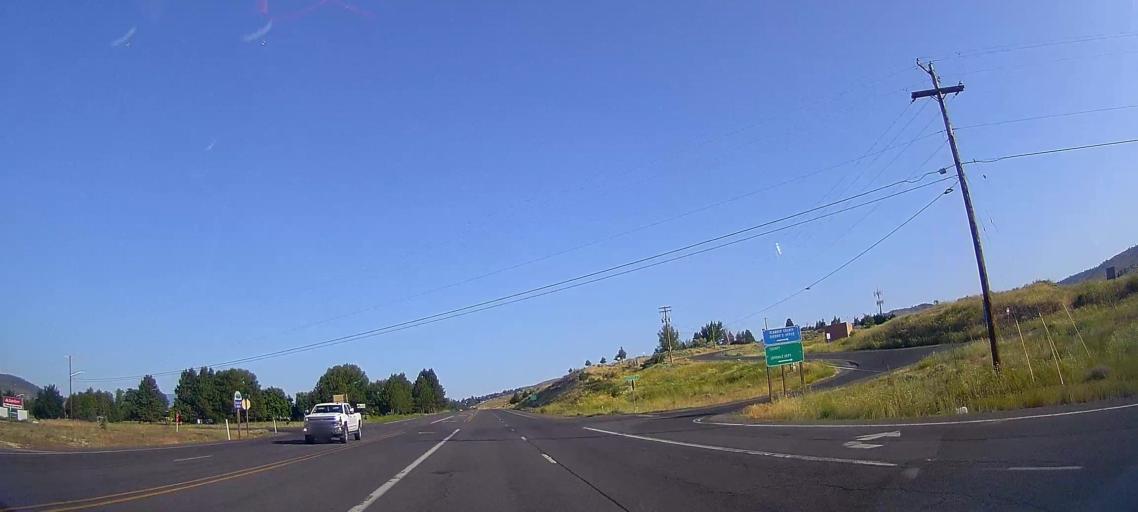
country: US
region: Oregon
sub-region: Klamath County
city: Altamont
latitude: 42.2171
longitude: -121.7470
